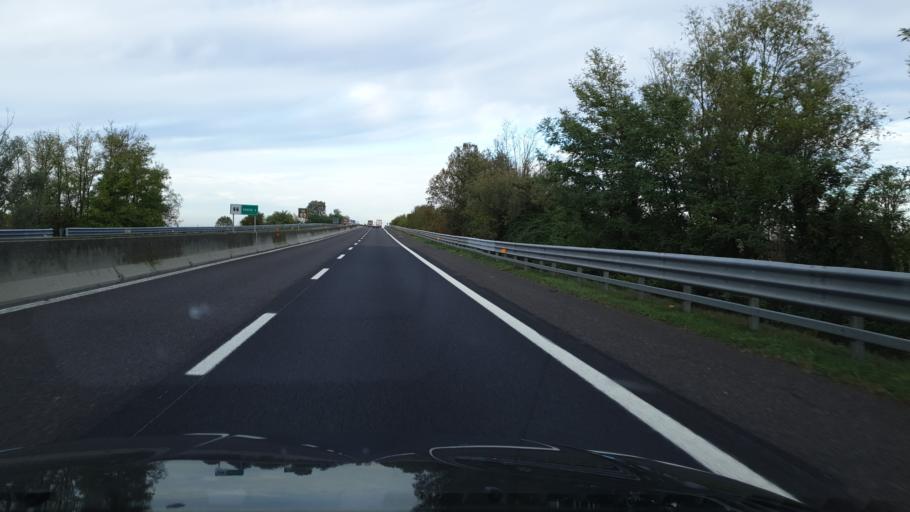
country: IT
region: Veneto
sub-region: Provincia di Rovigo
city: Costa di Rovigo
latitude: 45.0476
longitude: 11.7149
